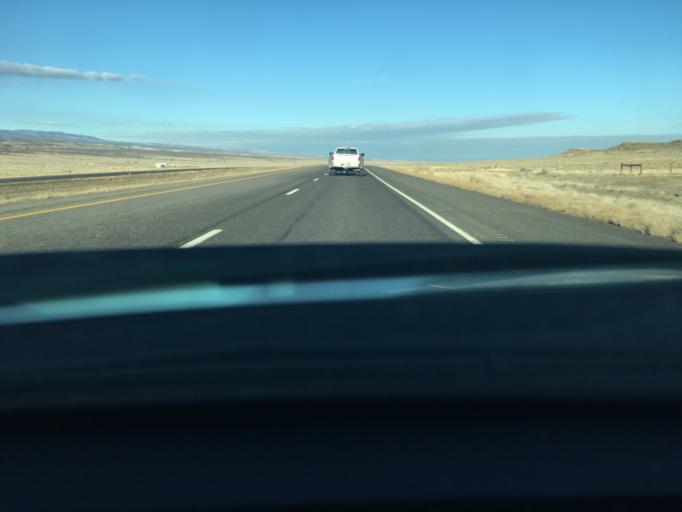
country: US
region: Colorado
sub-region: Mesa County
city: Palisade
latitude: 38.8736
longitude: -108.3411
